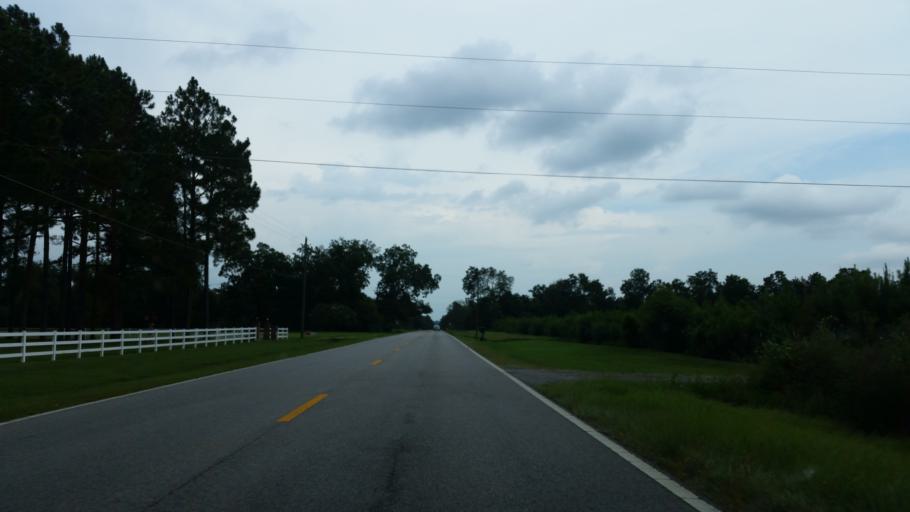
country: US
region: Florida
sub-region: Escambia County
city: Molino
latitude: 30.6809
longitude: -87.3702
